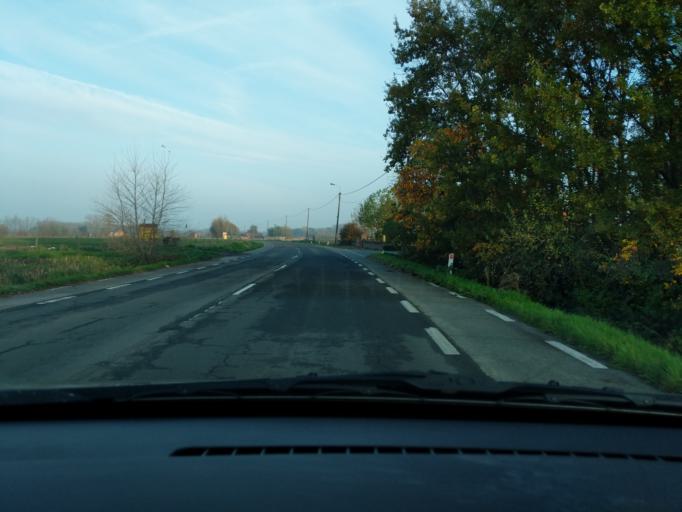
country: BE
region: Flanders
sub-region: Provincie West-Vlaanderen
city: Ruiselede
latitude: 51.0436
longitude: 3.4268
